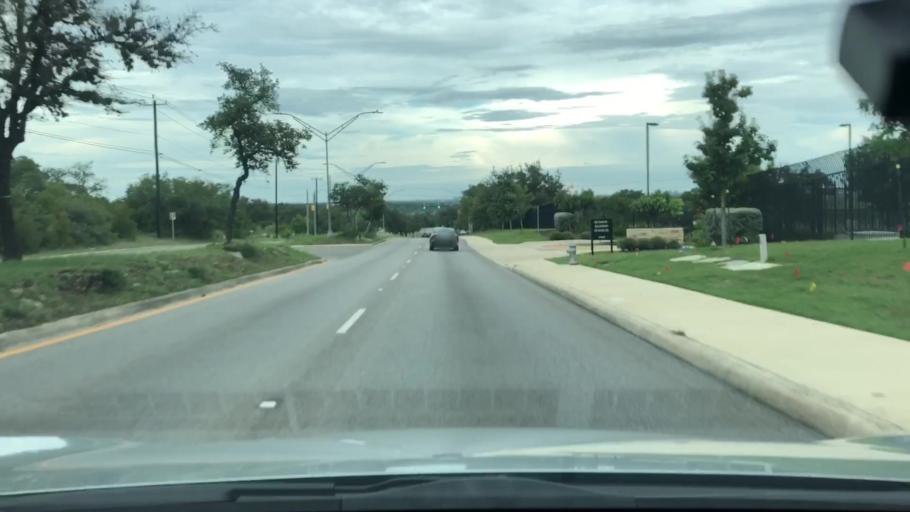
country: US
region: Texas
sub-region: Bexar County
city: Leon Valley
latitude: 29.4723
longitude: -98.6727
